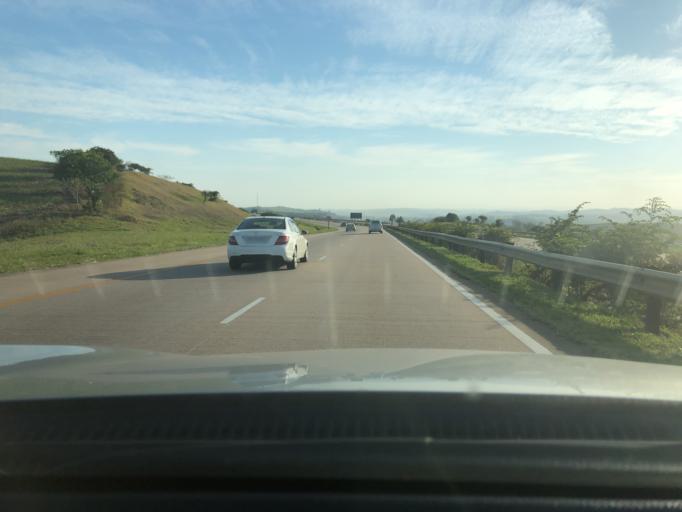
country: ZA
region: KwaZulu-Natal
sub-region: iLembe District Municipality
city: Stanger
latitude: -29.4371
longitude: 31.2658
